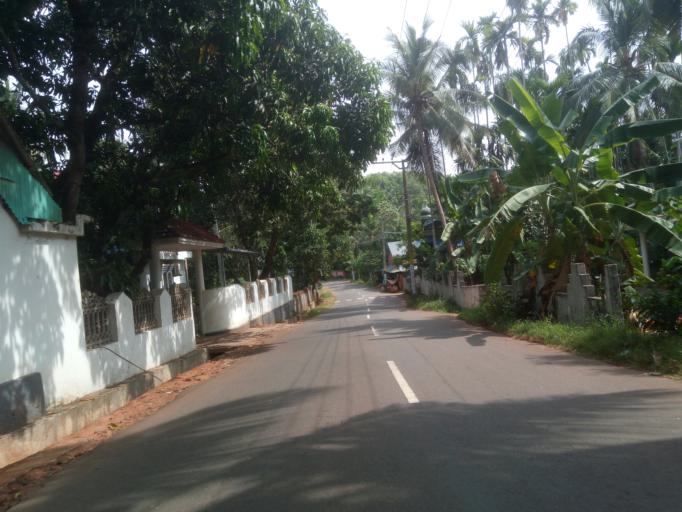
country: IN
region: Kerala
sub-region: Malappuram
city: Ponnani
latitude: 10.8181
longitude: 76.0234
